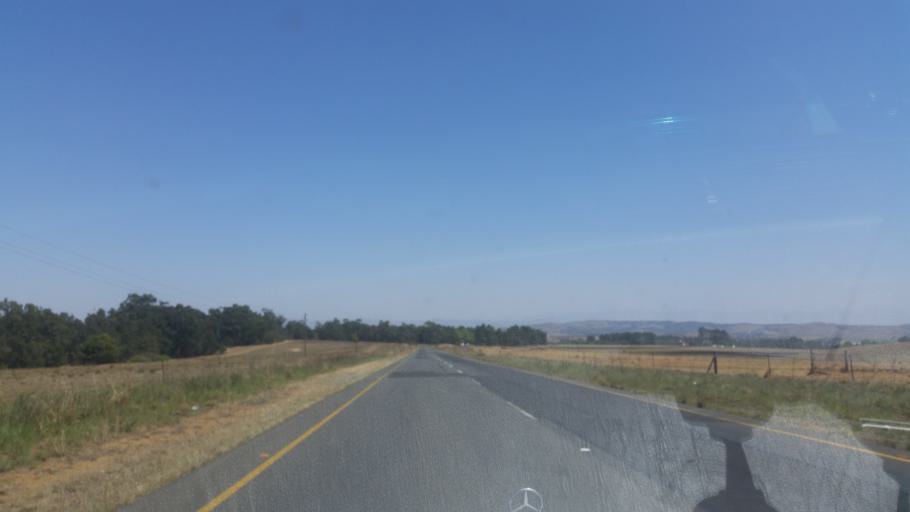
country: ZA
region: KwaZulu-Natal
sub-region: uMgungundlovu District Municipality
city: Mooirivier
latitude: -29.1460
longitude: 29.9901
